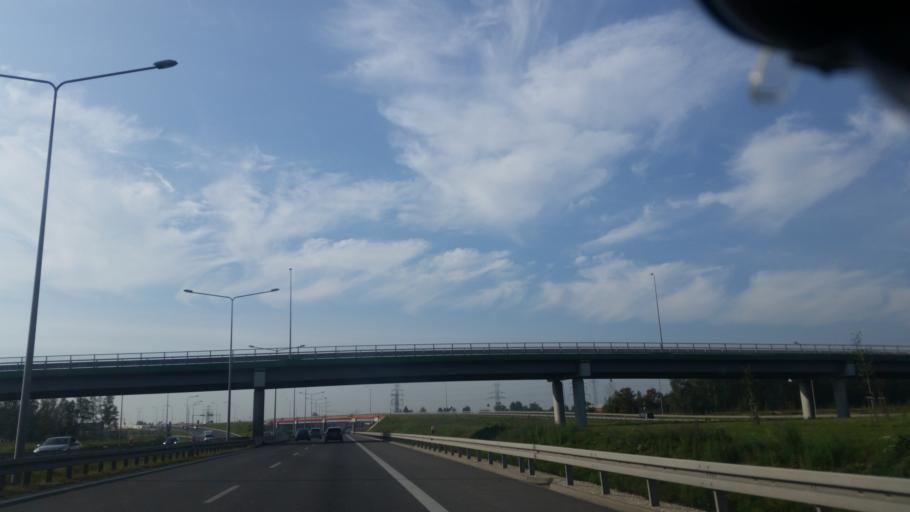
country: PL
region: Masovian Voivodeship
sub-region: Powiat pruszkowski
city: Nowe Grocholice
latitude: 52.1300
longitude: 20.8781
